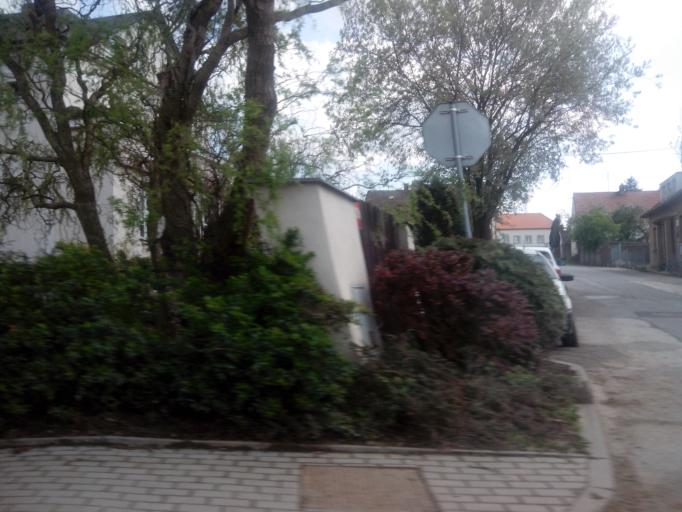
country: CZ
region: Central Bohemia
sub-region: Okres Beroun
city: Lodenice
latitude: 49.9842
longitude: 14.1280
